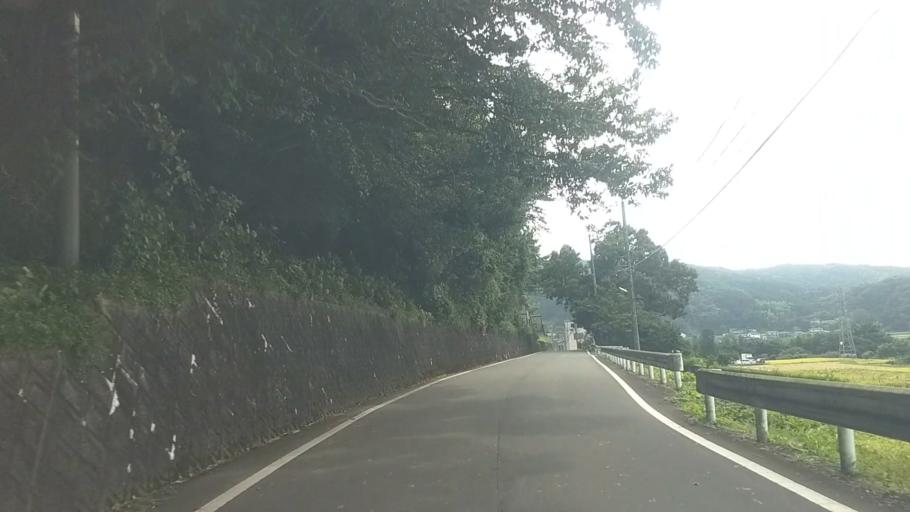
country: JP
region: Shizuoka
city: Ito
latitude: 34.9730
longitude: 138.9748
